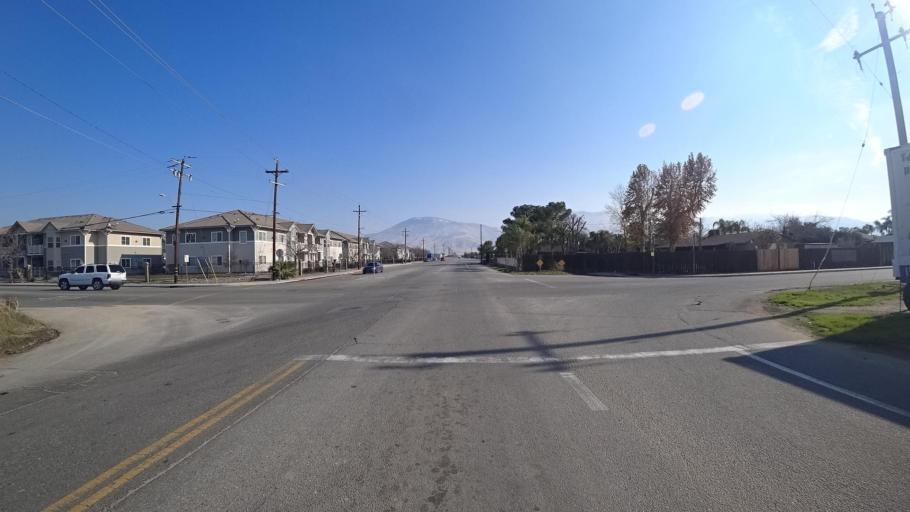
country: US
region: California
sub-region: Kern County
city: Arvin
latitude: 35.1945
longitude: -118.8333
